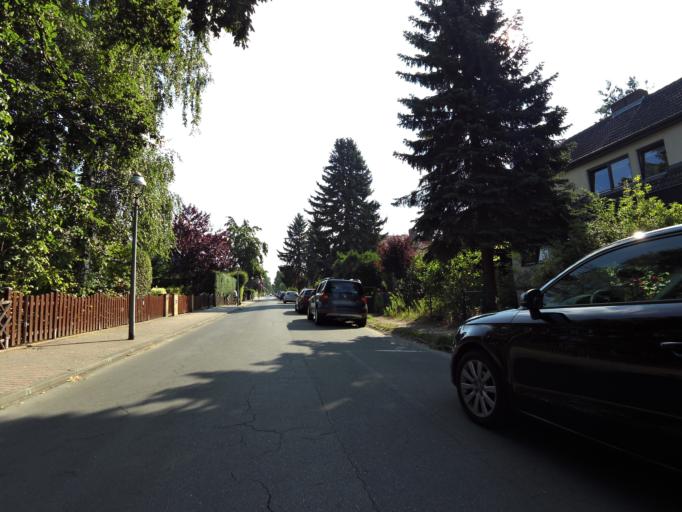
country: DE
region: Berlin
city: Lichtenrade
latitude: 52.3992
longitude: 13.4134
